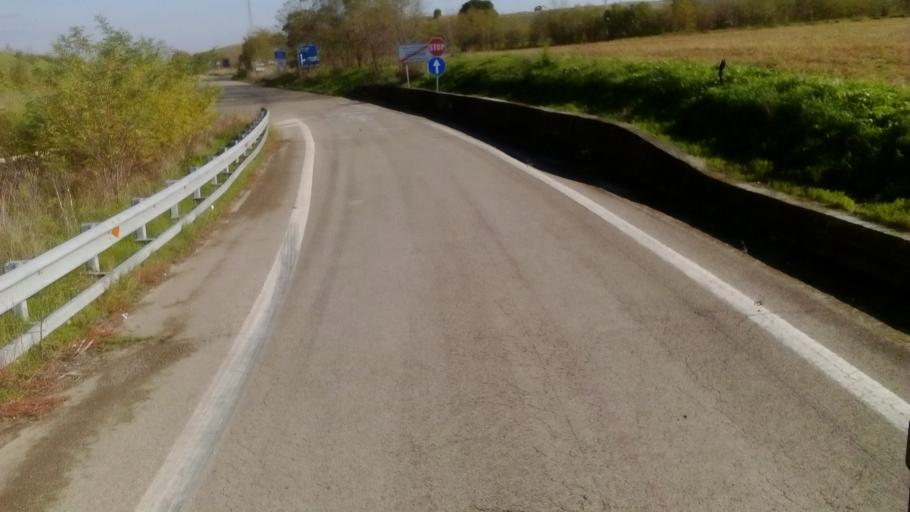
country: IT
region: Basilicate
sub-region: Provincia di Potenza
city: Melfi
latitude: 41.0648
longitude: 15.6781
